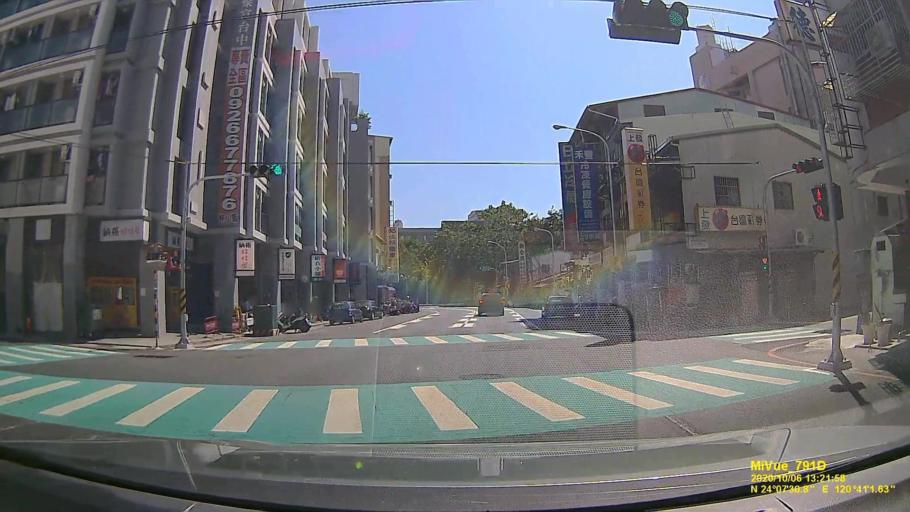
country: TW
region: Taiwan
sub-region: Taichung City
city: Taichung
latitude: 24.1252
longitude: 120.6838
